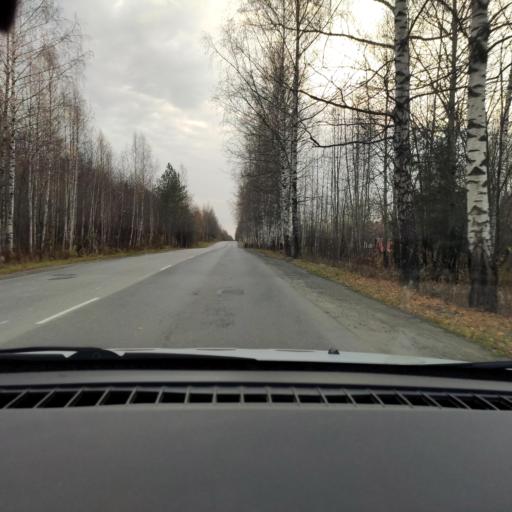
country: RU
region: Perm
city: Polazna
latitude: 58.1052
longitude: 56.4170
